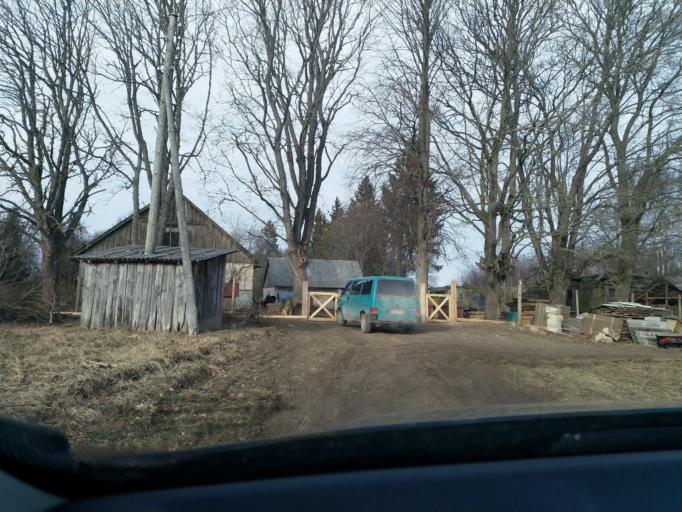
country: LV
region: Kuldigas Rajons
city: Kuldiga
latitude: 57.0466
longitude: 21.8559
